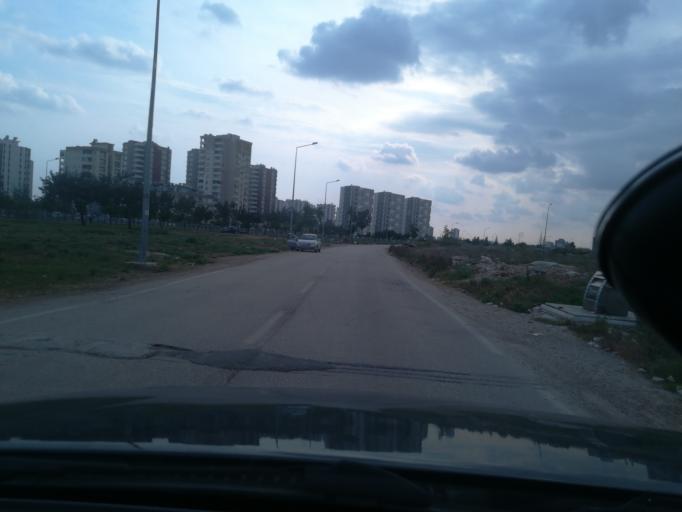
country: TR
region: Adana
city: Seyhan
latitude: 37.0102
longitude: 35.2715
